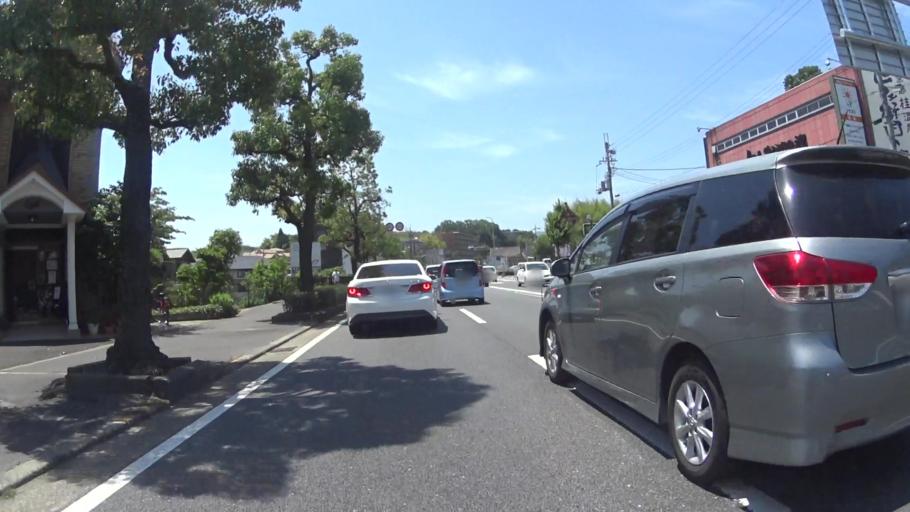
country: JP
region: Kyoto
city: Kameoka
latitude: 35.0477
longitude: 135.5453
